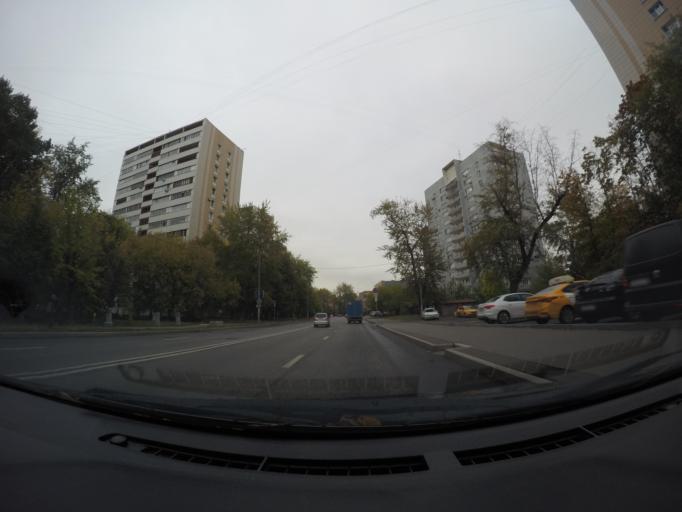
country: RU
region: Moscow
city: Lefortovo
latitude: 55.7791
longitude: 37.7250
